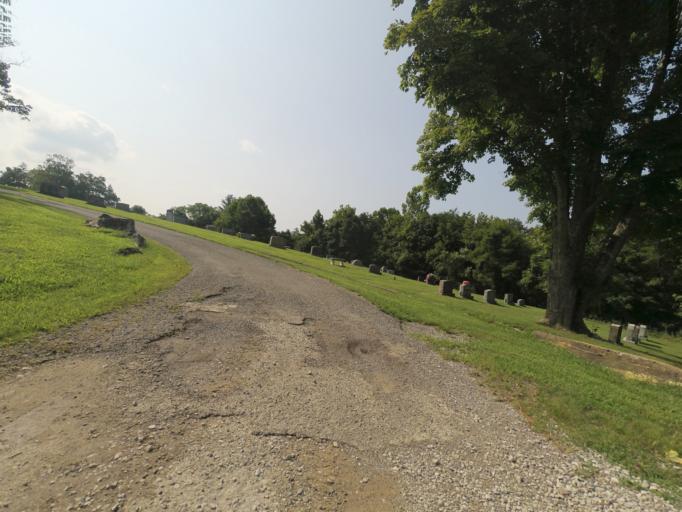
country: US
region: West Virginia
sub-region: Cabell County
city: Huntington
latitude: 38.4049
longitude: -82.3947
